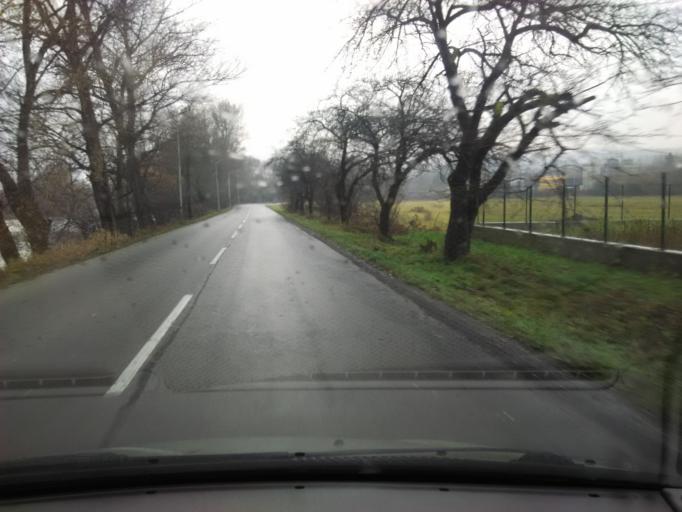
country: SK
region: Zilinsky
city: Bytca
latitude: 49.2172
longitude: 18.5423
